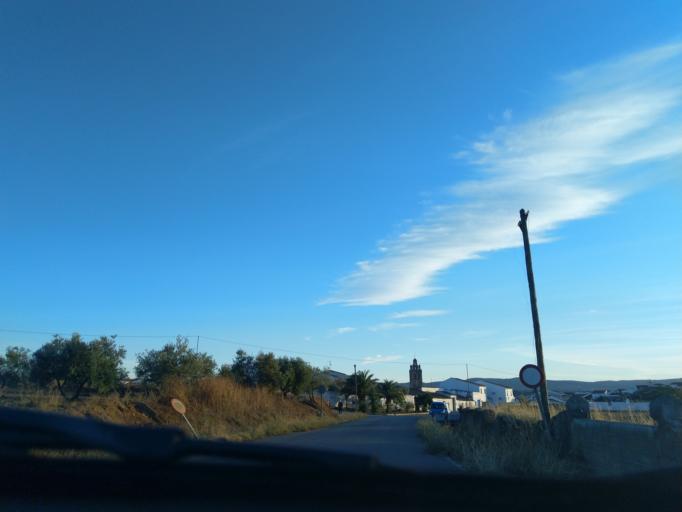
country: ES
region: Extremadura
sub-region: Provincia de Badajoz
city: Valverde de Llerena
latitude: 38.2172
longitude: -5.8214
